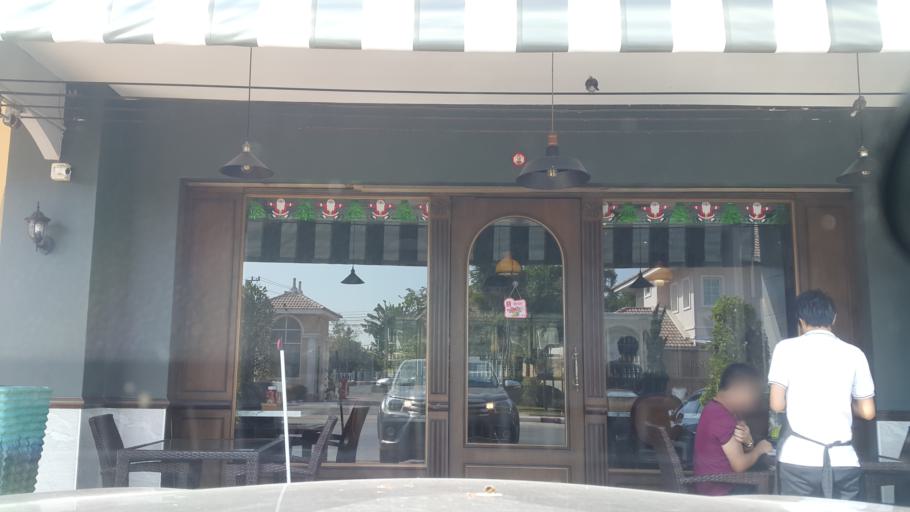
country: TH
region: Nakhon Ratchasima
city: Nakhon Ratchasima
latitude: 14.9849
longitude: 102.0573
